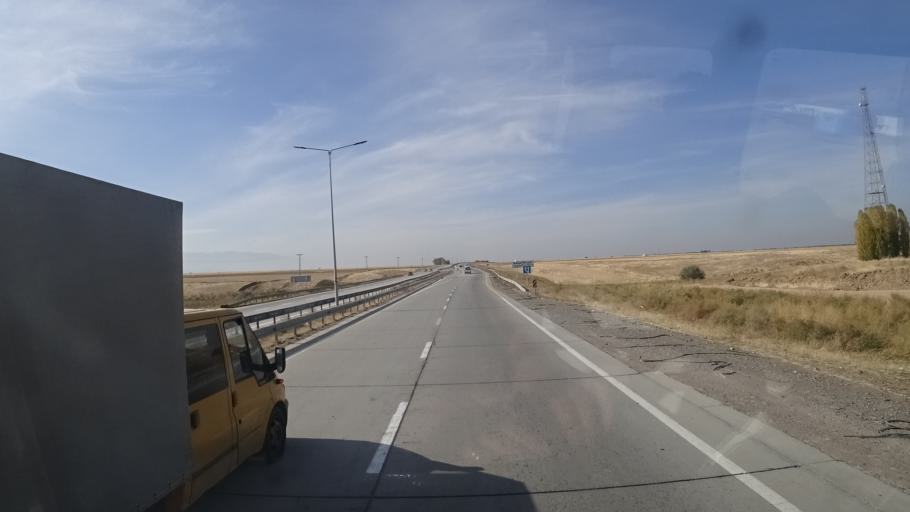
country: KZ
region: Zhambyl
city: Merke
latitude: 42.8897
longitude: 72.9821
